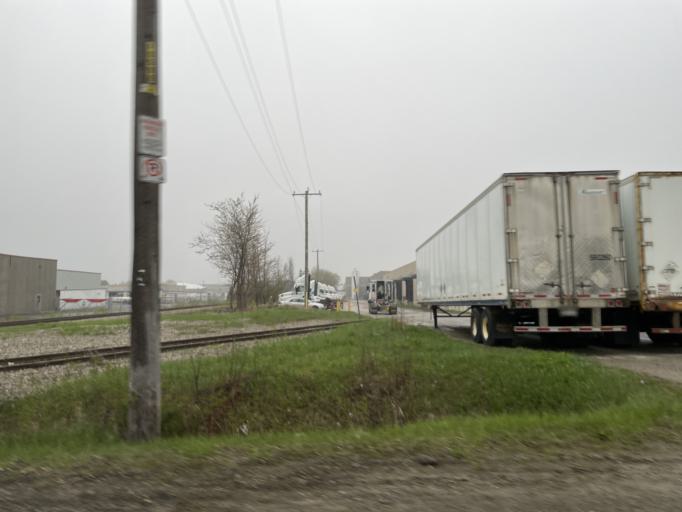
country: CA
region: Ontario
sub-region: Wellington County
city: Guelph
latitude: 43.5448
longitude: -80.3010
